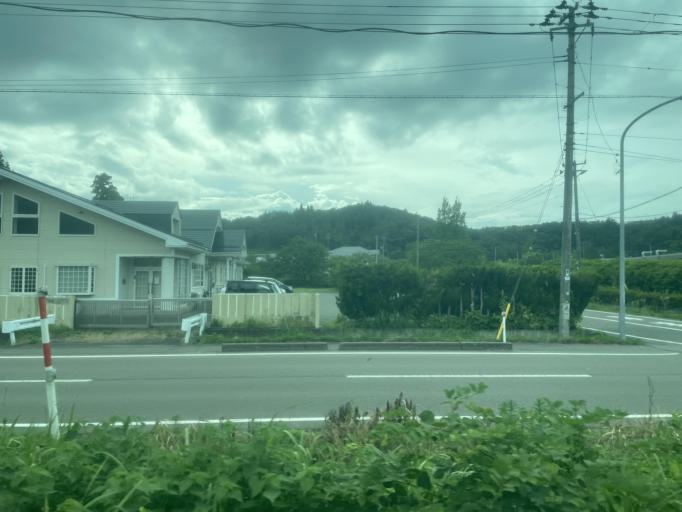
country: JP
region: Niigata
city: Nagaoka
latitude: 37.5371
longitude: 138.7189
